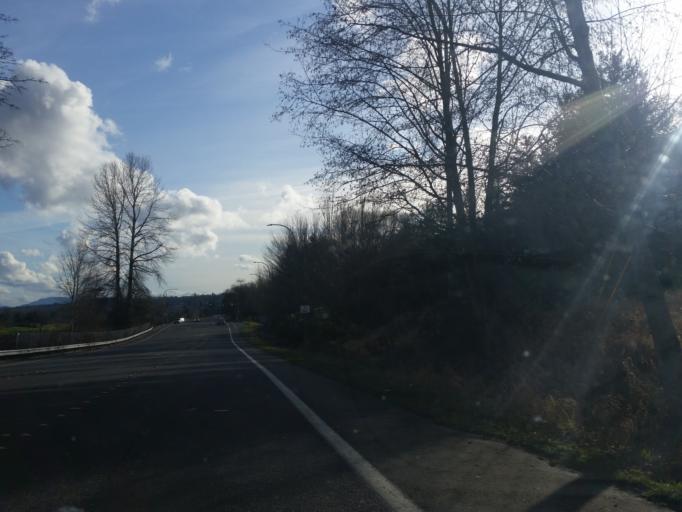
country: US
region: Washington
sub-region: King County
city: Kingsgate
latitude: 47.7065
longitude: -122.1538
